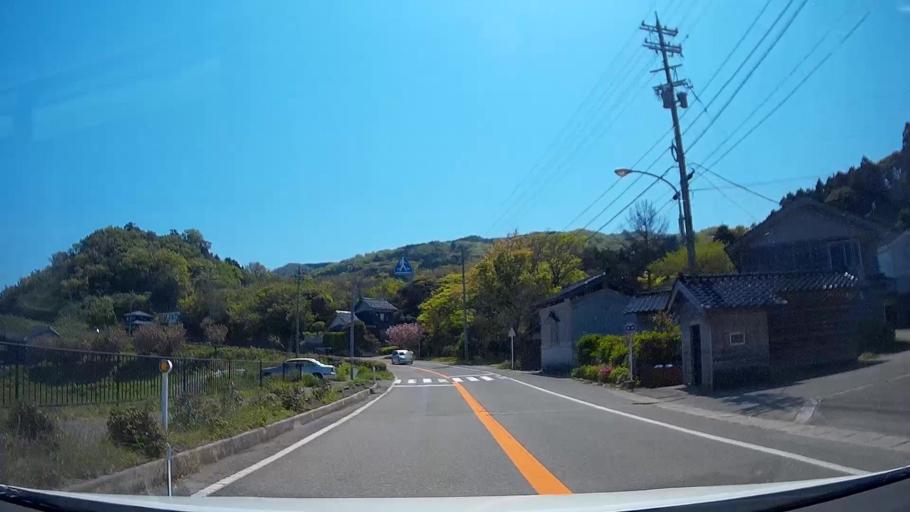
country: JP
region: Ishikawa
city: Nanao
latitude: 37.4001
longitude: 136.9408
